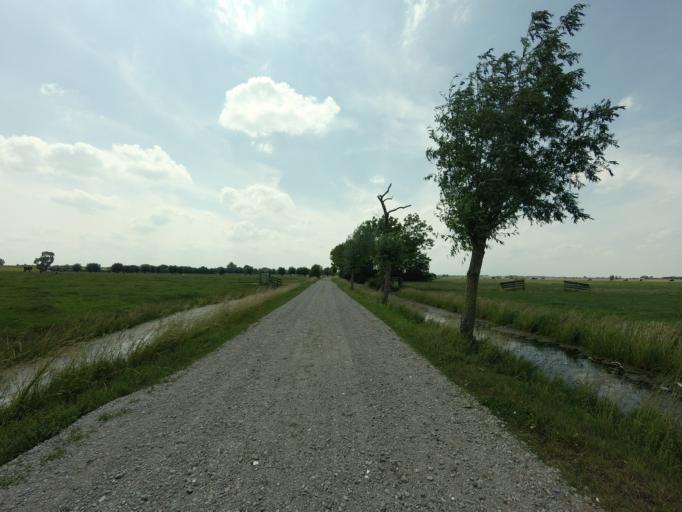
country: NL
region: Utrecht
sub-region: Gemeente Lopik
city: Lopik
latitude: 51.9511
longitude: 4.9157
